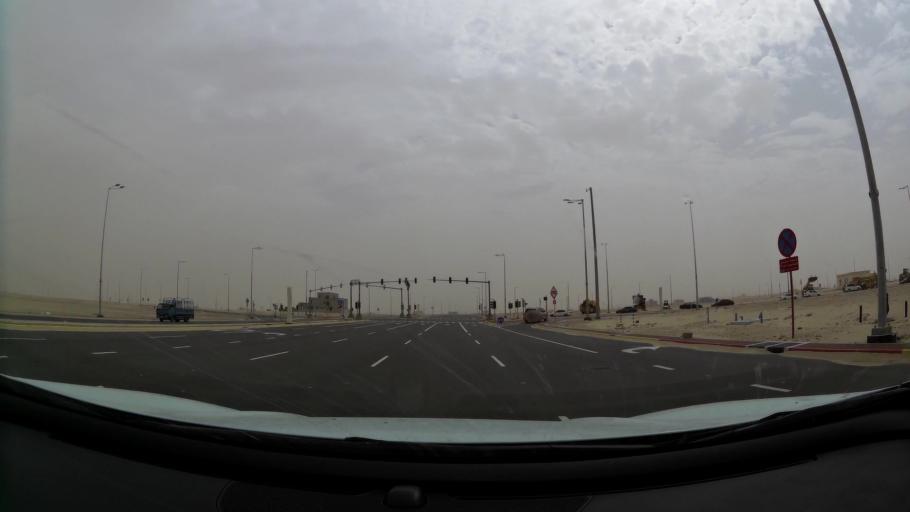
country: AE
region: Abu Dhabi
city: Abu Dhabi
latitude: 24.3708
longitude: 54.7462
